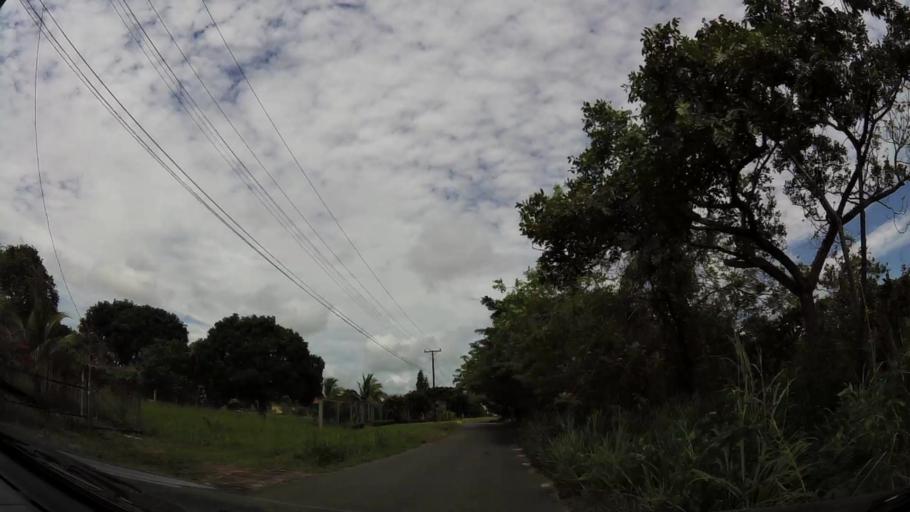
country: PA
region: Panama
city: Nueva Gorgona
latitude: 8.5281
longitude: -79.9156
